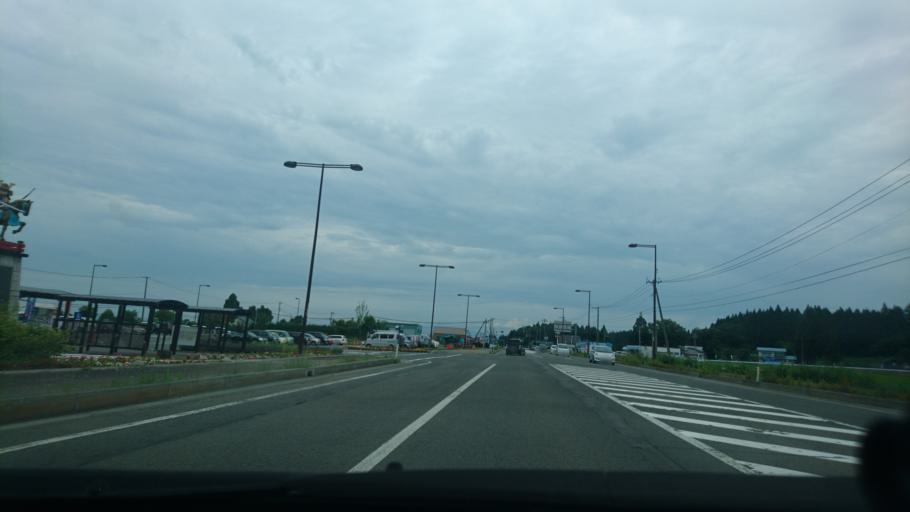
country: JP
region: Akita
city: Yokotemachi
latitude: 39.3792
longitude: 140.5681
